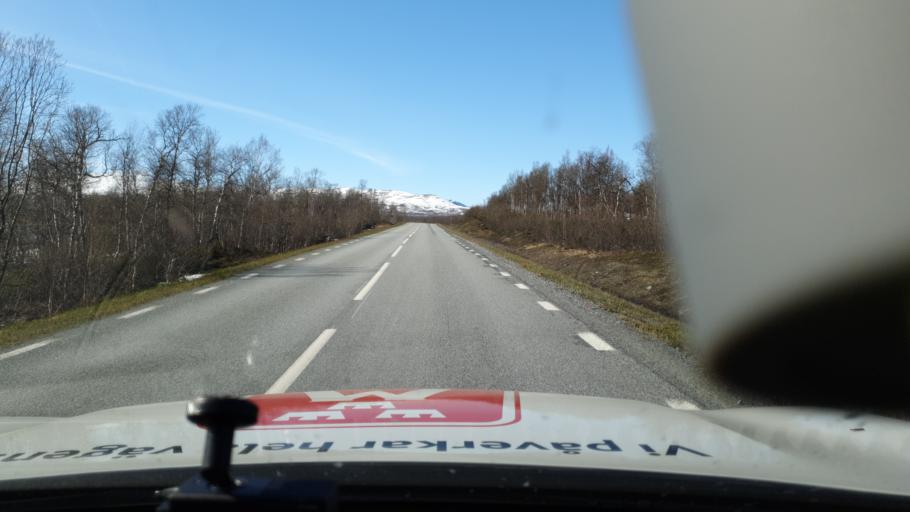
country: NO
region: Nordland
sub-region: Rana
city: Mo i Rana
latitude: 66.0190
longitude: 15.0900
